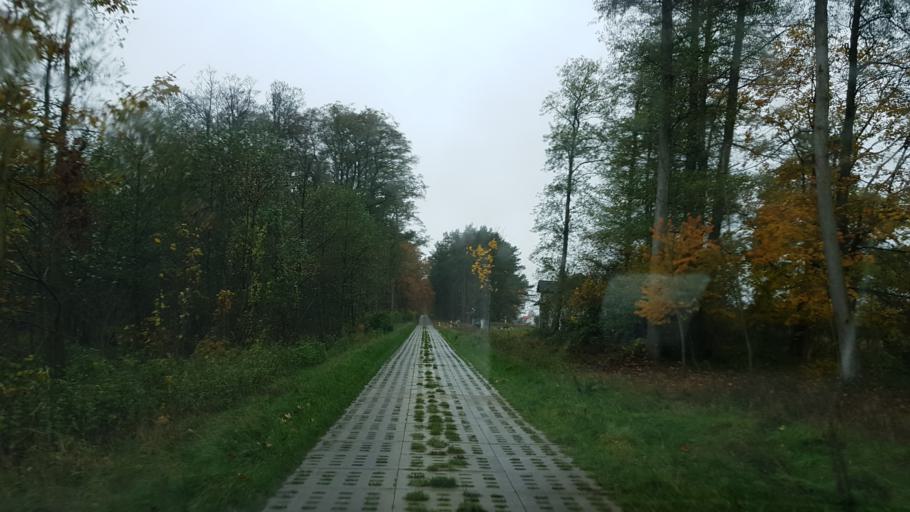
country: PL
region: West Pomeranian Voivodeship
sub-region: Powiat goleniowski
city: Goleniow
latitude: 53.5792
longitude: 14.7891
